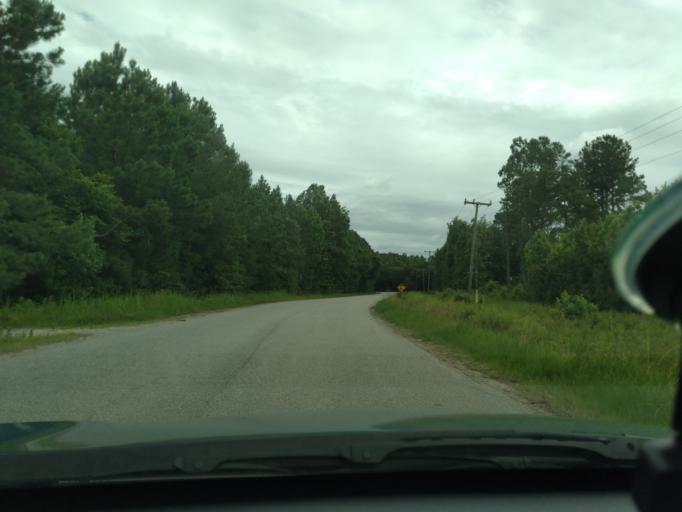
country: US
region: North Carolina
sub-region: Washington County
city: Plymouth
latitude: 35.8713
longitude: -76.7121
